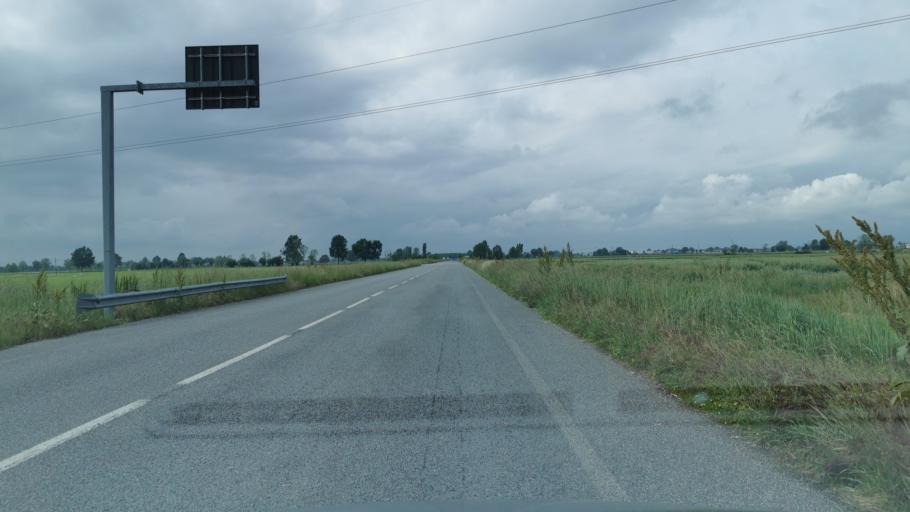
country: IT
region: Piedmont
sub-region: Provincia di Cuneo
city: Racconigi
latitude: 44.7613
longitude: 7.6967
